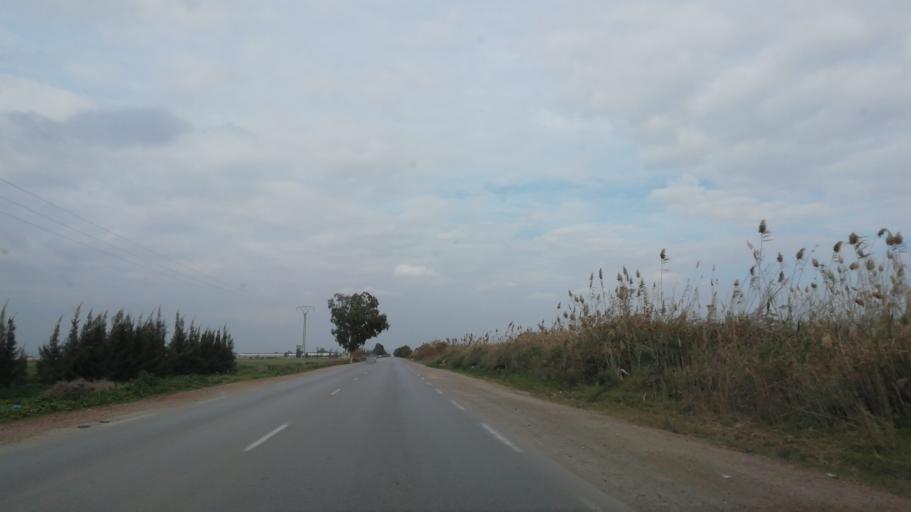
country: DZ
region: Mascara
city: Mascara
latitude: 35.6452
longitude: 0.0600
